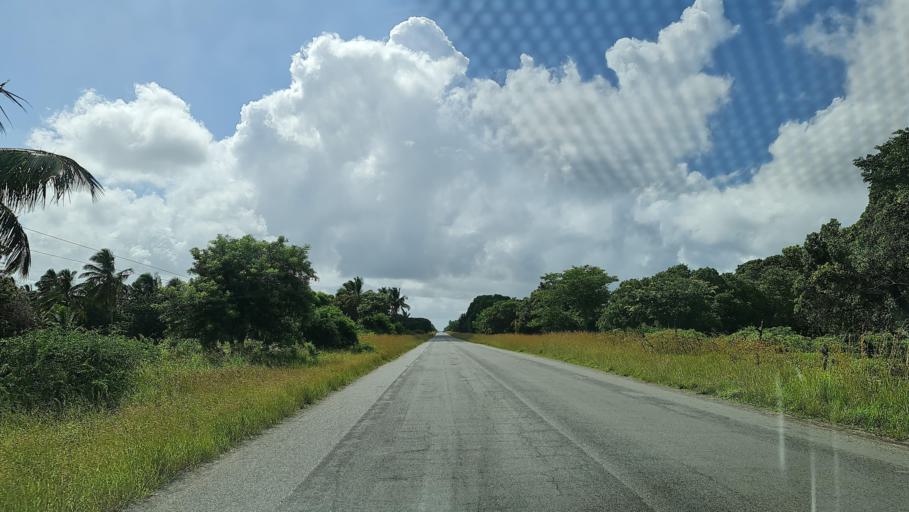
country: MZ
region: Gaza
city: Manjacaze
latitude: -24.6778
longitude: 34.5934
